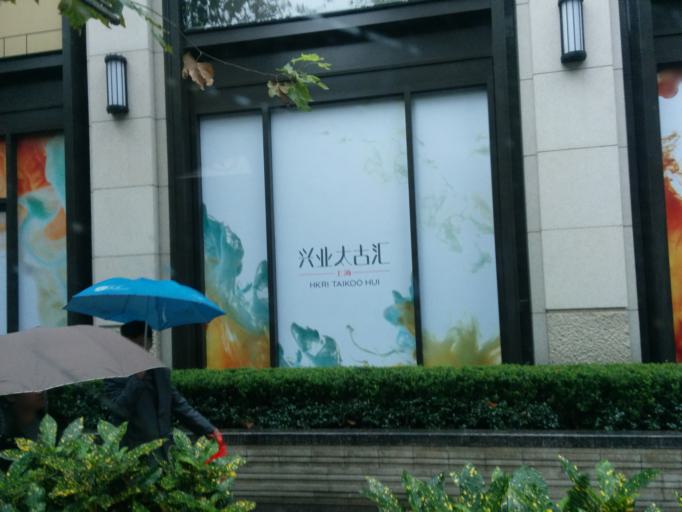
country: CN
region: Shanghai Shi
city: Shanghai
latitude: 31.2329
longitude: 121.4585
